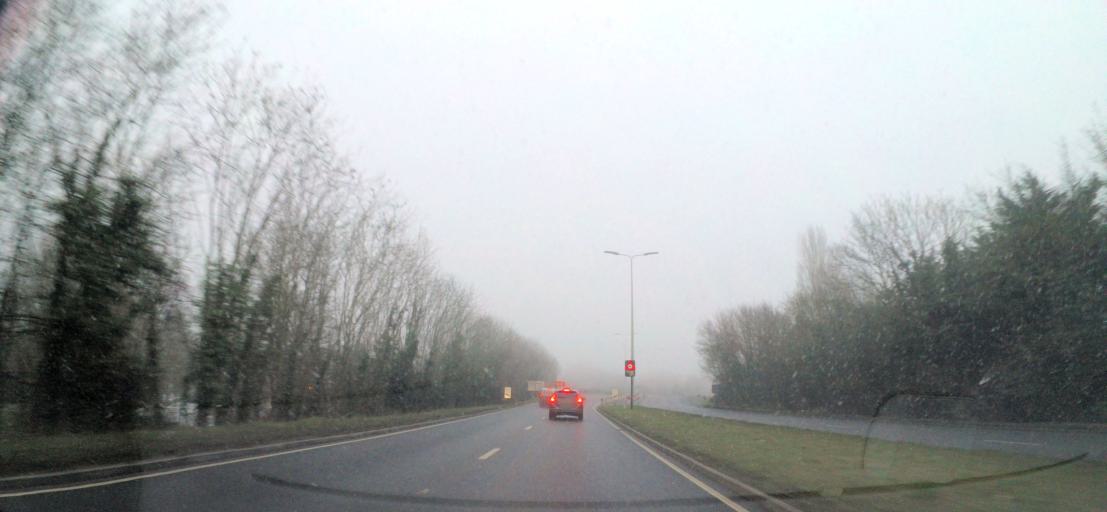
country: GB
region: England
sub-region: West Berkshire
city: Theale
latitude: 51.4365
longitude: -1.0736
